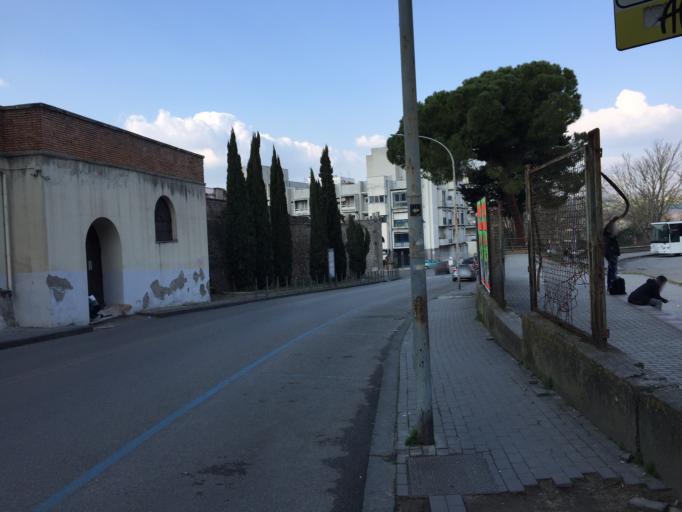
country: IT
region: Campania
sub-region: Provincia di Benevento
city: Benevento
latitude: 41.1311
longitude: 14.7826
